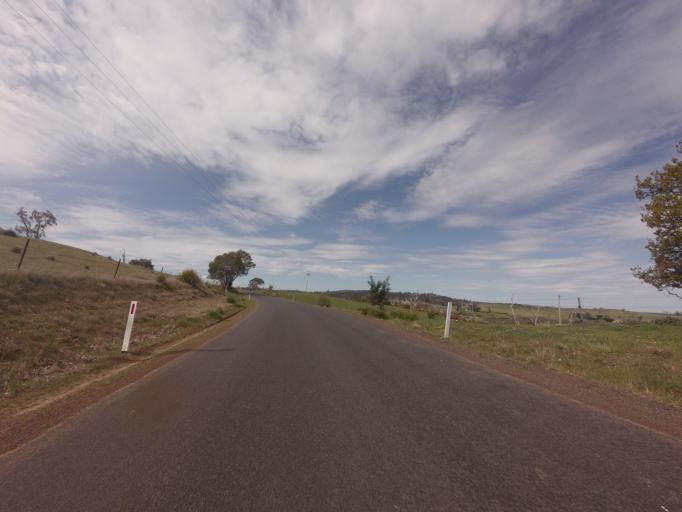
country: AU
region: Tasmania
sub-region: Northern Midlands
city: Evandale
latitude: -41.8867
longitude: 147.3820
